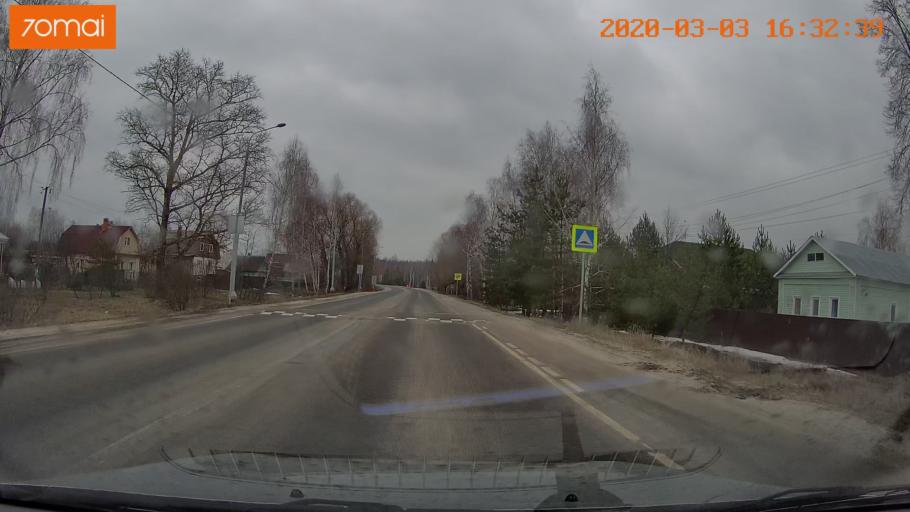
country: RU
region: Moskovskaya
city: Konobeyevo
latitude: 55.4196
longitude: 38.7342
